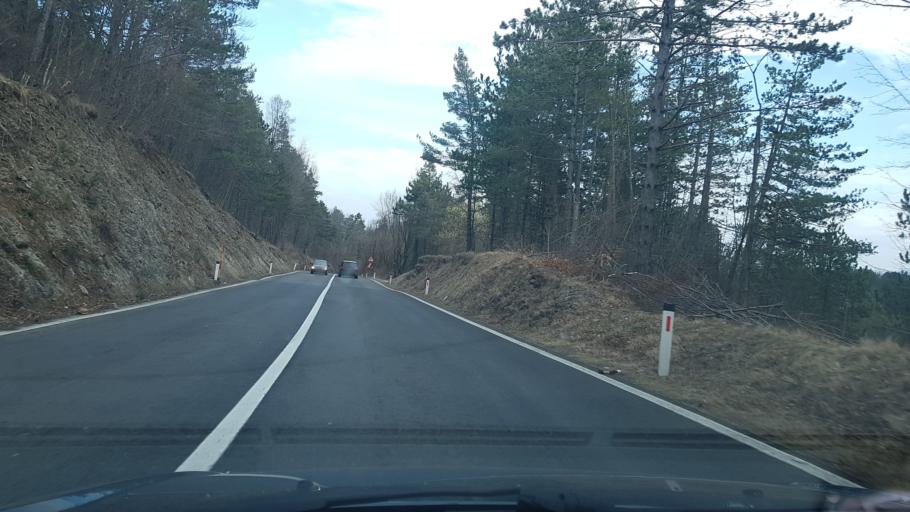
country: SI
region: Ilirska Bistrica
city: Ilirska Bistrica
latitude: 45.4913
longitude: 14.2063
